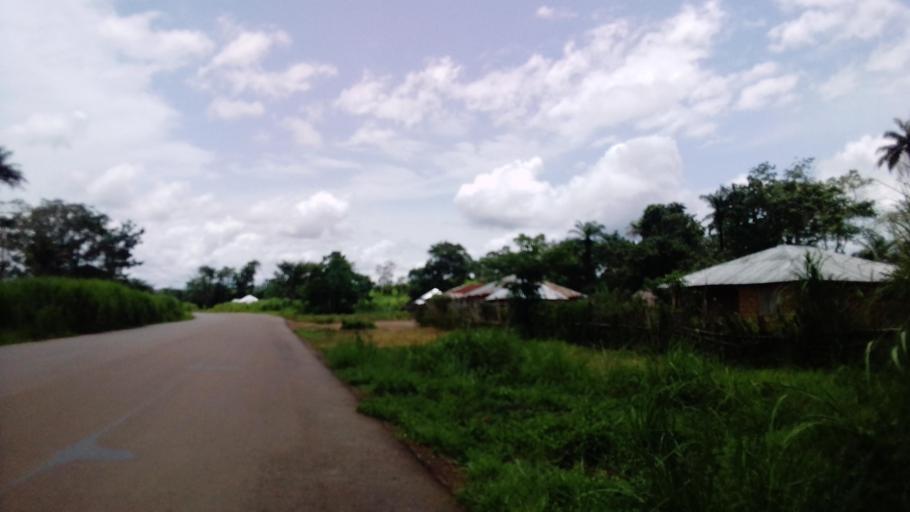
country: SL
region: Northern Province
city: Makeni
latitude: 9.0656
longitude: -12.1767
